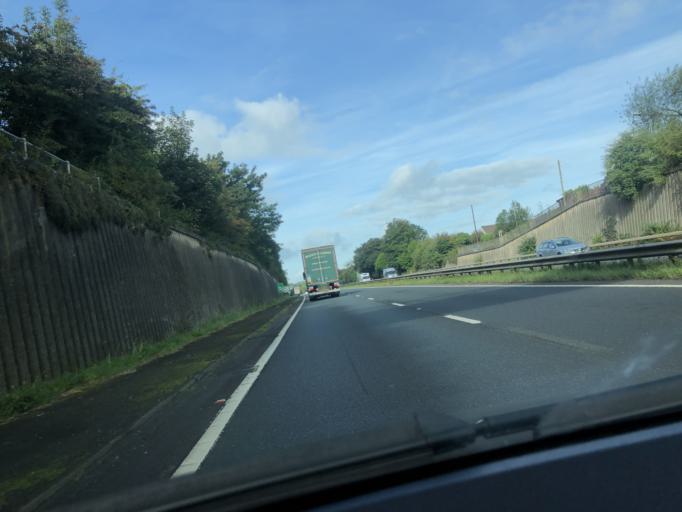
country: GB
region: England
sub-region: Cornwall
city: Launceston
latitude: 50.6286
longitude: -4.3596
